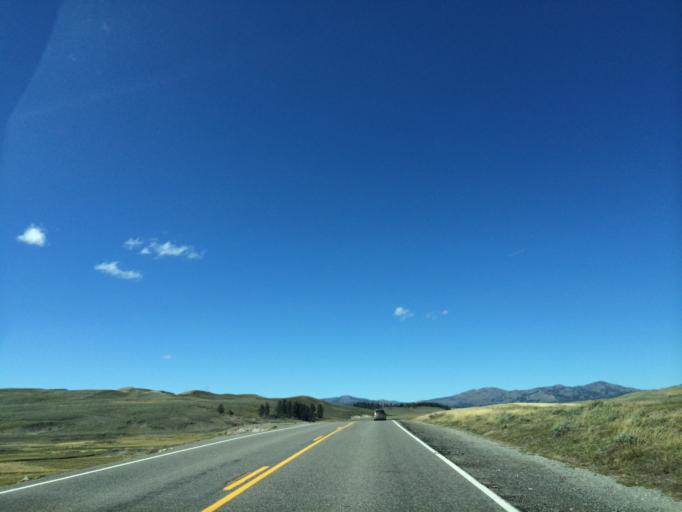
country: US
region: Montana
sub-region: Gallatin County
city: West Yellowstone
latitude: 44.6427
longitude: -110.4568
